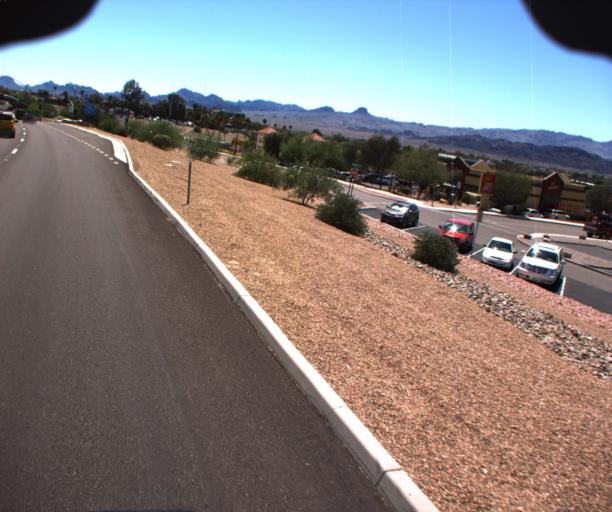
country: US
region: Arizona
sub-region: Mohave County
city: Lake Havasu City
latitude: 34.4757
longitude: -114.3477
